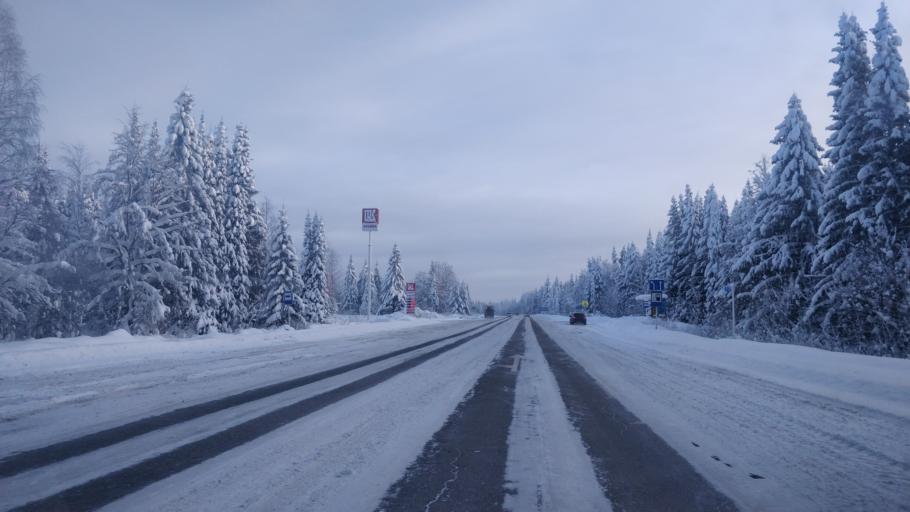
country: RU
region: Perm
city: Polazna
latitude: 58.3012
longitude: 56.5990
